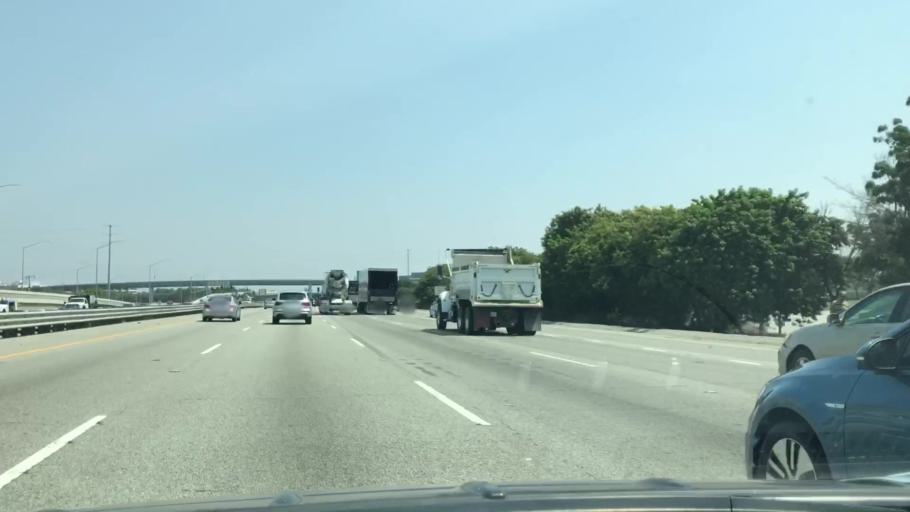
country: US
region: California
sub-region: Santa Clara County
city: Santa Clara
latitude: 37.3752
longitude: -121.9350
